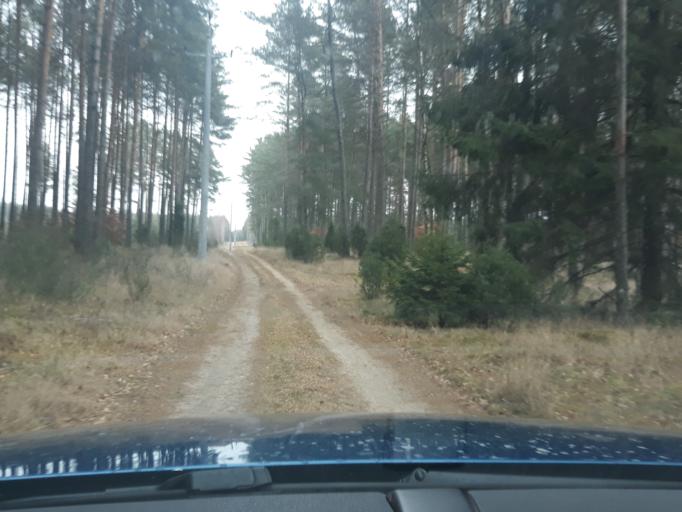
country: PL
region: Pomeranian Voivodeship
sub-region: Powiat czluchowski
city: Czluchow
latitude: 53.8201
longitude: 17.4279
